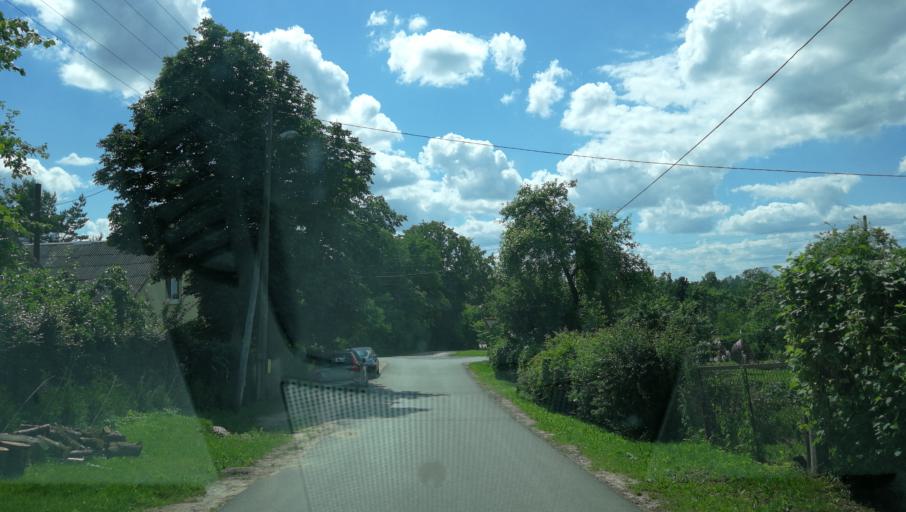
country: LV
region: Broceni
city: Broceni
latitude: 56.6746
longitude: 22.5678
